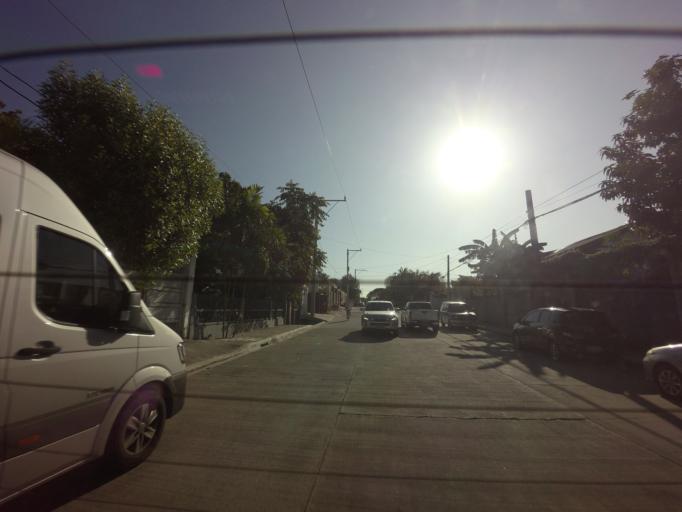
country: PH
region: Metro Manila
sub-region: Makati City
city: Makati City
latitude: 14.5304
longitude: 121.0365
